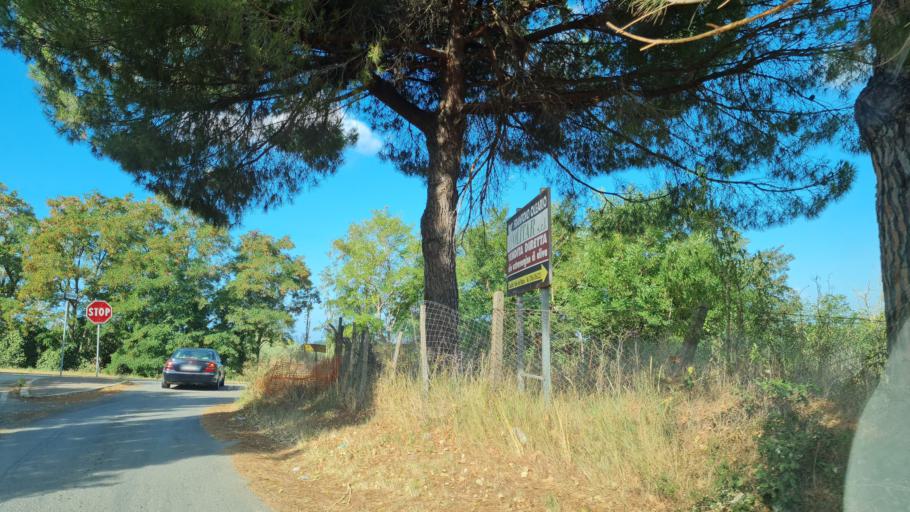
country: IT
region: Latium
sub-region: Provincia di Viterbo
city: Tarquinia
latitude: 42.2558
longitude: 11.7445
